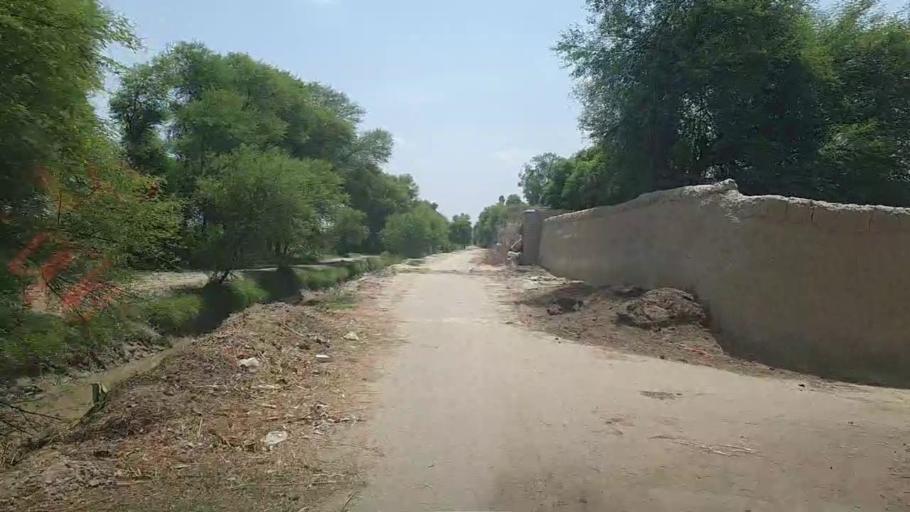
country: PK
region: Sindh
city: Ubauro
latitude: 28.2788
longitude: 69.8088
